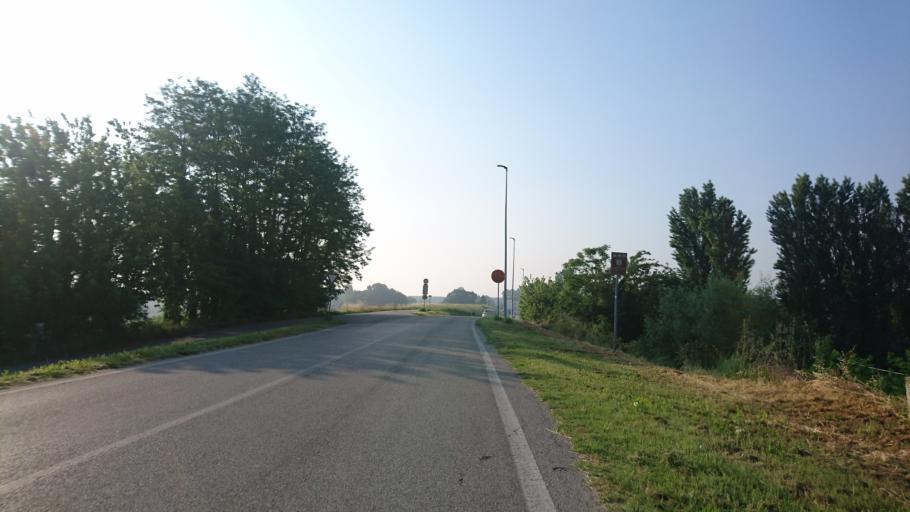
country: IT
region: Lombardy
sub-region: Provincia di Mantova
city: Sermide
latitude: 45.0102
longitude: 11.2961
